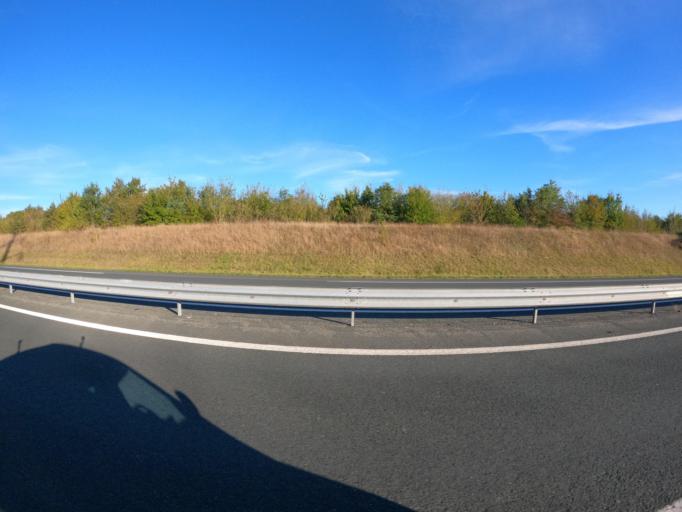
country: FR
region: Pays de la Loire
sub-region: Departement de Maine-et-Loire
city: Mazieres-en-Mauges
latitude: 47.0545
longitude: -0.8338
